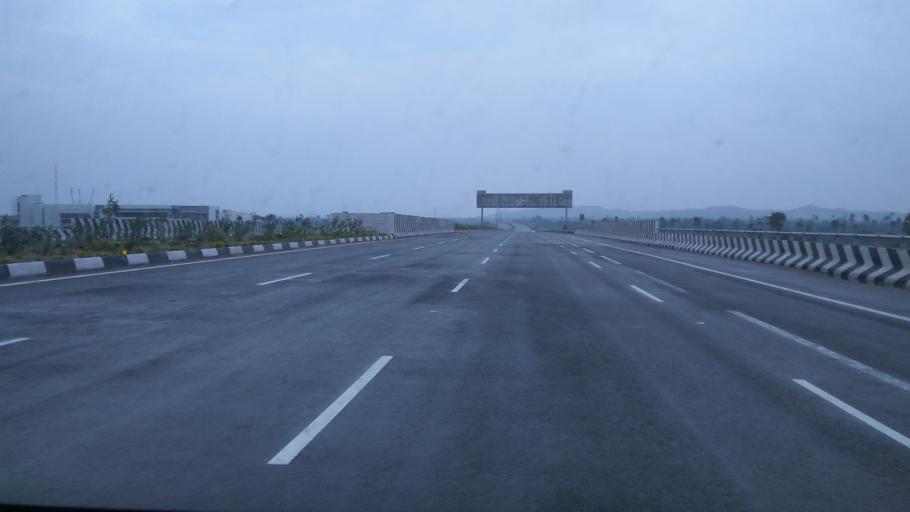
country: IN
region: Telangana
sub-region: Rangareddi
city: Ghatkesar
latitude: 17.4527
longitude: 78.6686
